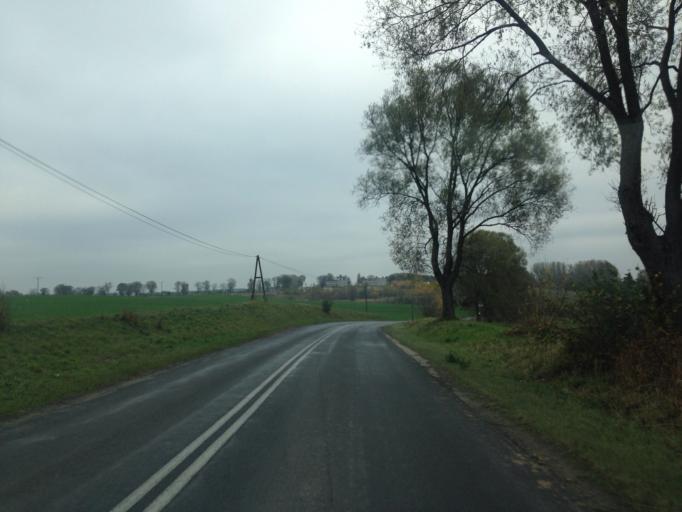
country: PL
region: Kujawsko-Pomorskie
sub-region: Powiat brodnicki
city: Jablonowo Pomorskie
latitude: 53.3515
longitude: 19.2054
